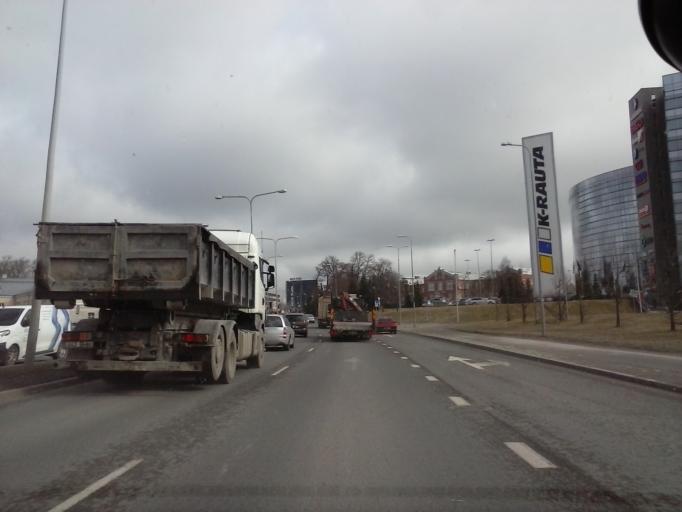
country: EE
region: Harju
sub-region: Tallinna linn
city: Tallinn
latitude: 59.4022
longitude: 24.7143
